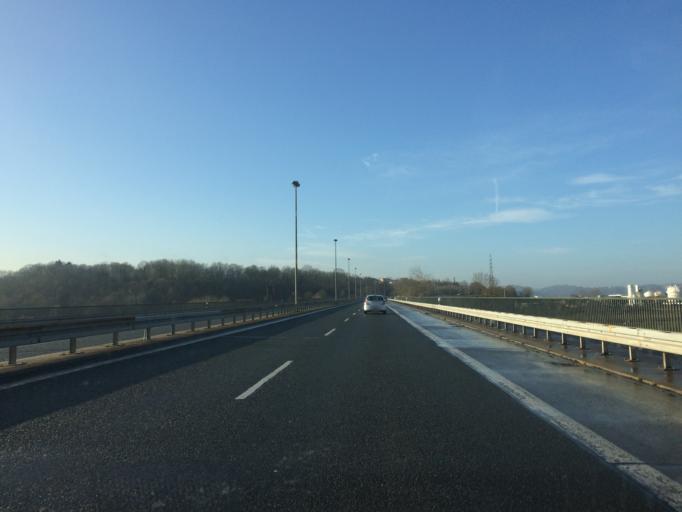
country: DE
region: North Rhine-Westphalia
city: Hattingen
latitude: 51.4213
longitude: 7.2104
